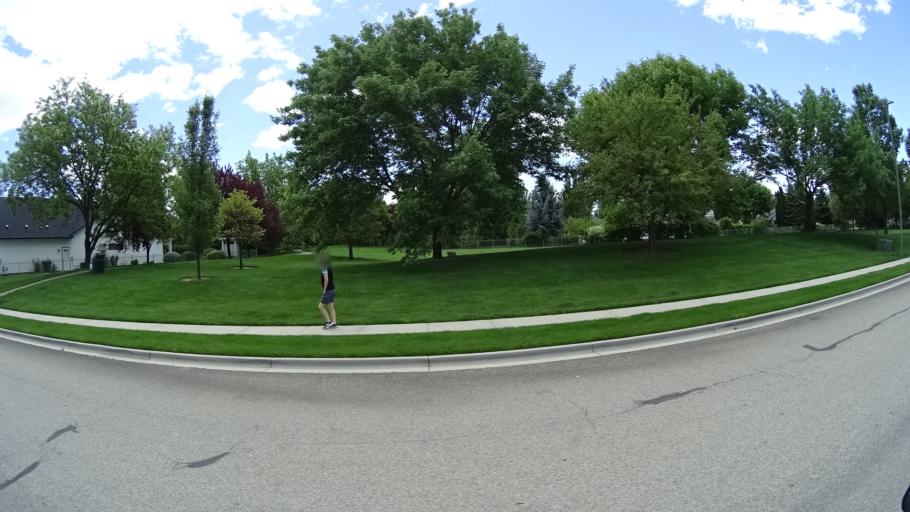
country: US
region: Idaho
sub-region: Ada County
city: Eagle
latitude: 43.6524
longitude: -116.3471
